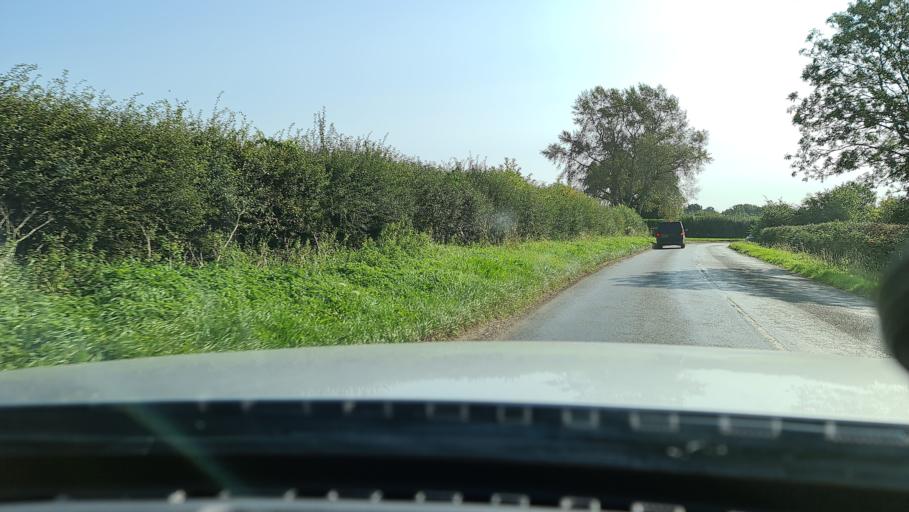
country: GB
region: England
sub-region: Oxfordshire
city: Adderbury
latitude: 52.0296
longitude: -1.2831
